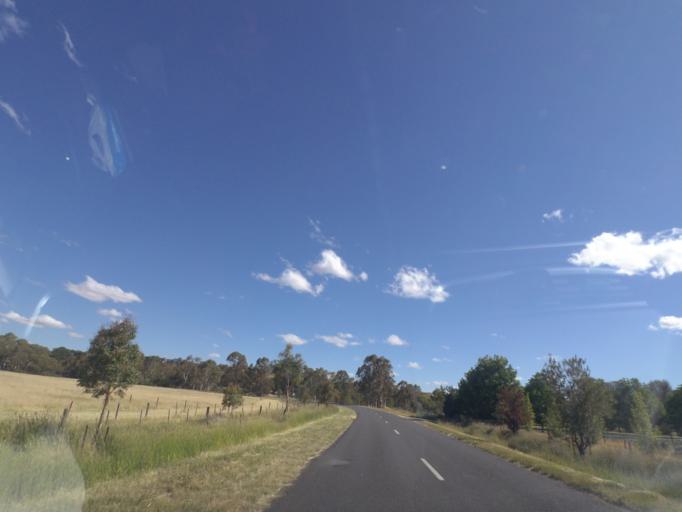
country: AU
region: Victoria
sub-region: Hume
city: Craigieburn
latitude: -37.3989
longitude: 144.8912
